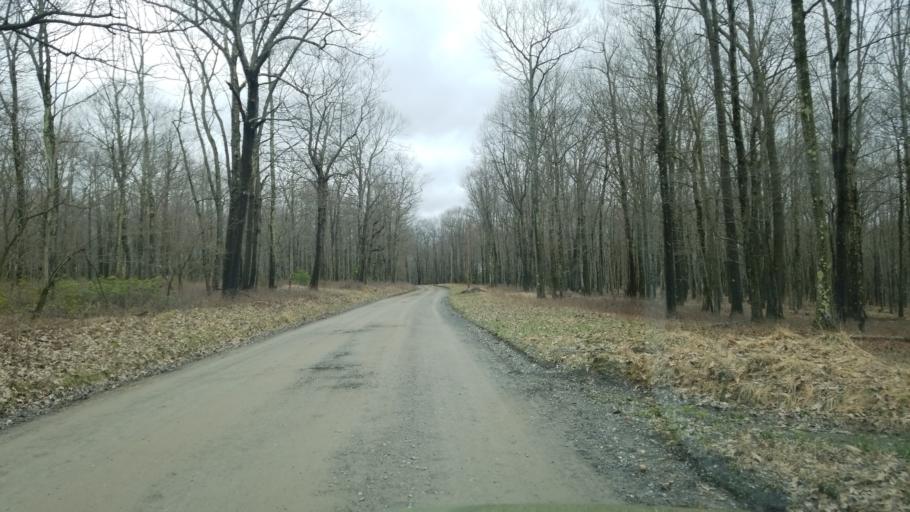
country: US
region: Pennsylvania
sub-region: Clearfield County
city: Shiloh
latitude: 41.1594
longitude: -78.3344
